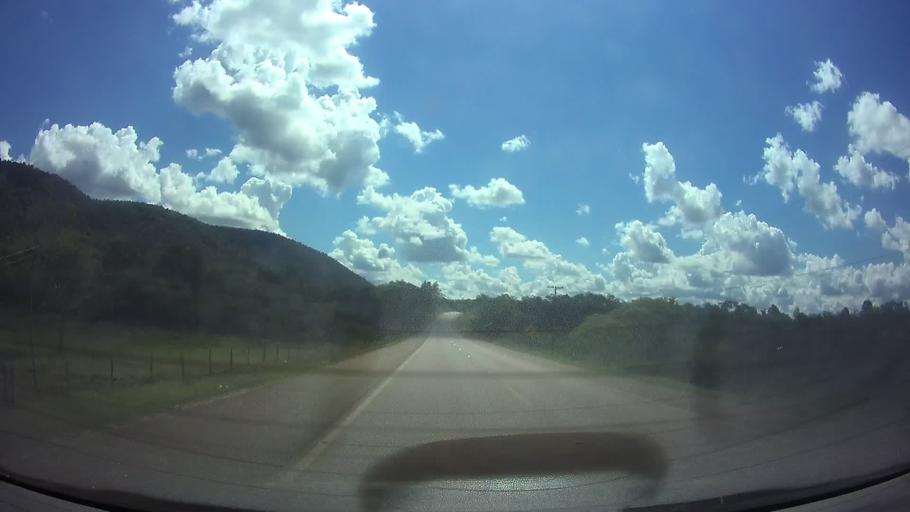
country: PY
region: Paraguari
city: La Colmena
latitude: -25.9176
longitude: -56.7334
